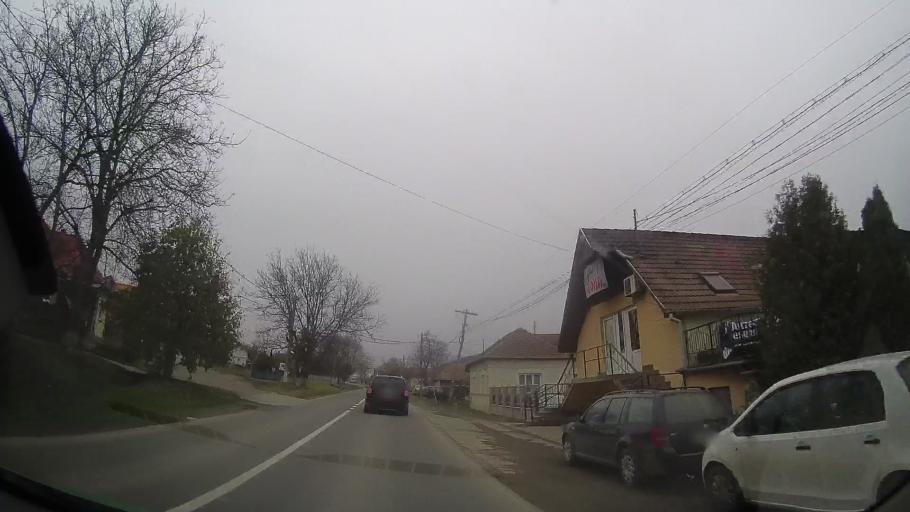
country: RO
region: Mures
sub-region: Comuna Ceausu de Campie
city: Ceausu de Campie
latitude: 46.6081
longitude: 24.5294
